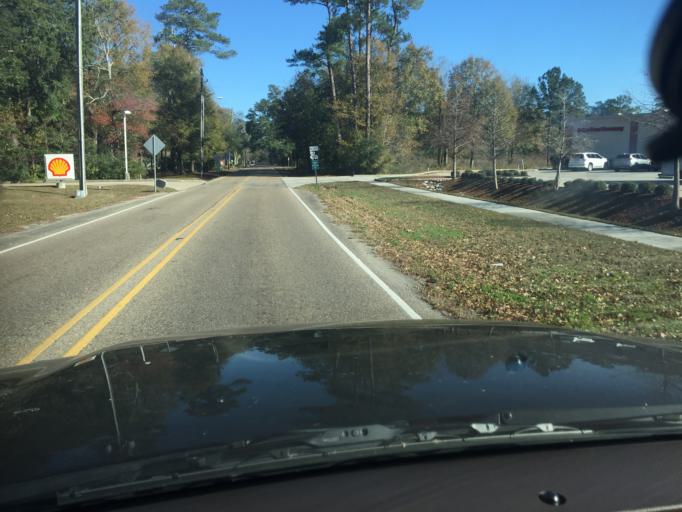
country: US
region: Louisiana
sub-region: Saint Tammany Parish
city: Slidell
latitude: 30.3107
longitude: -89.7475
